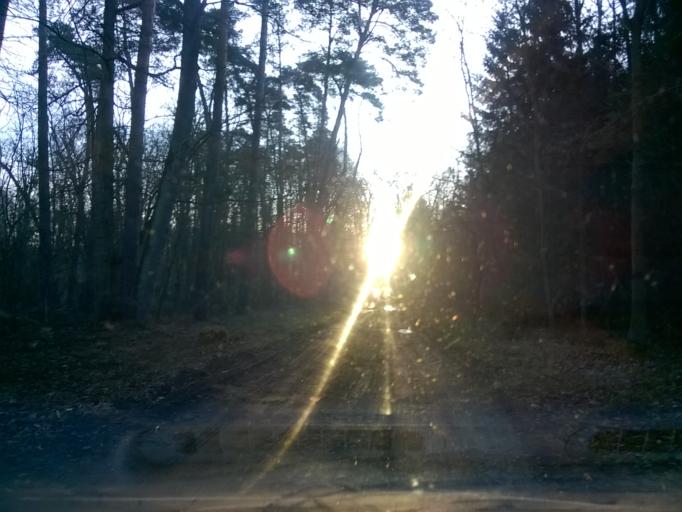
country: PL
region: Kujawsko-Pomorskie
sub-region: Powiat nakielski
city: Sadki
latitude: 53.1203
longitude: 17.3969
